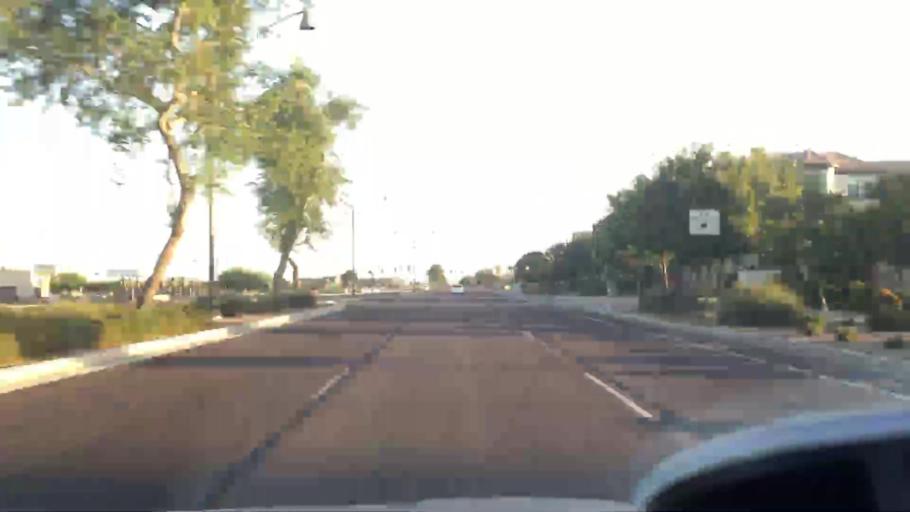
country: US
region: Arizona
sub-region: Maricopa County
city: Gilbert
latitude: 33.3190
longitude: -111.7211
